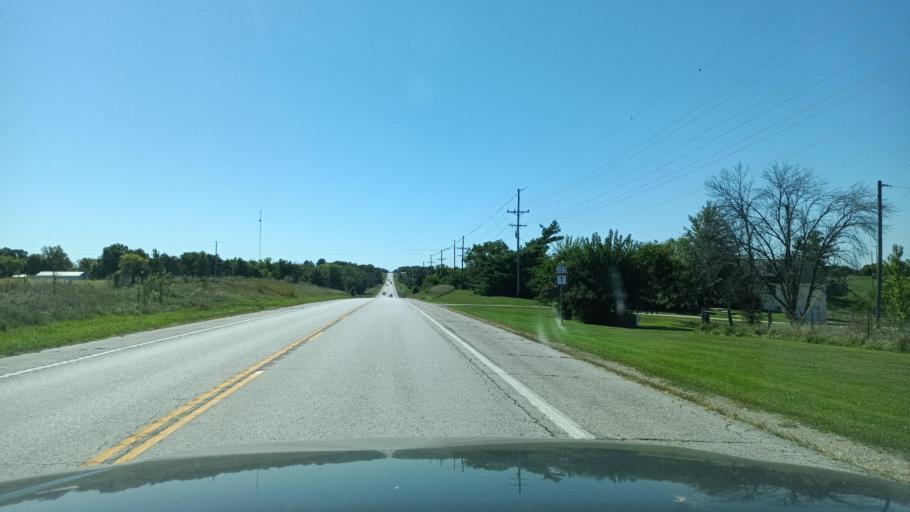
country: US
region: Missouri
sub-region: Adair County
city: Kirksville
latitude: 40.2744
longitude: -92.5825
